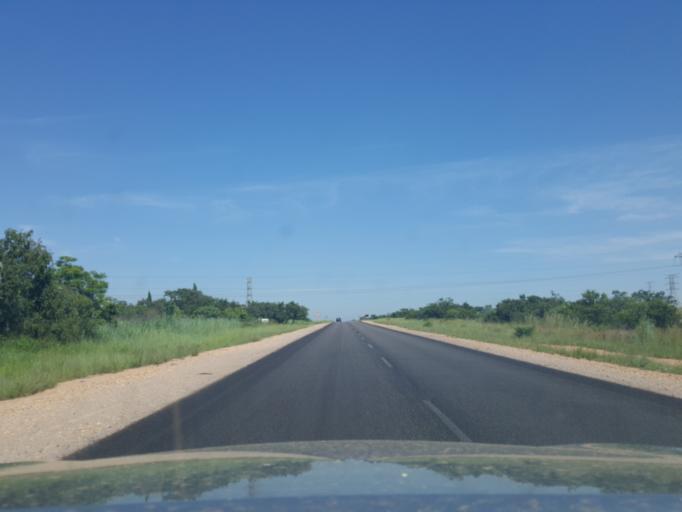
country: ZA
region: Gauteng
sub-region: City of Tshwane Metropolitan Municipality
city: Cullinan
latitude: -25.6840
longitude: 28.4647
